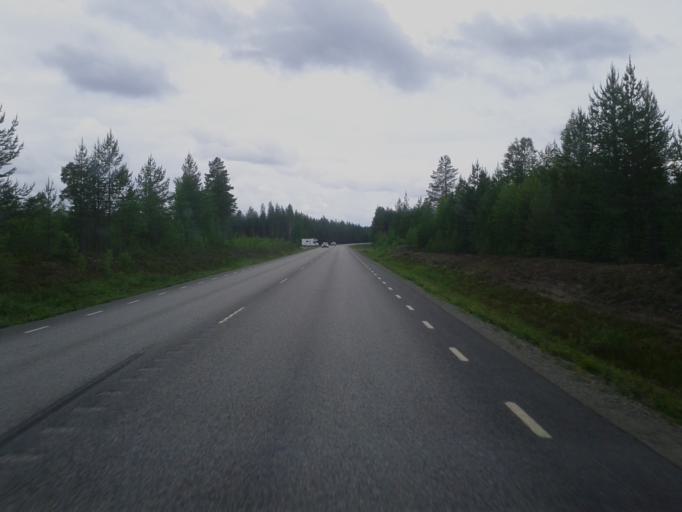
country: SE
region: Vaesterbotten
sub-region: Skelleftea Kommun
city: Langsele
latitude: 64.9335
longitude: 19.9650
